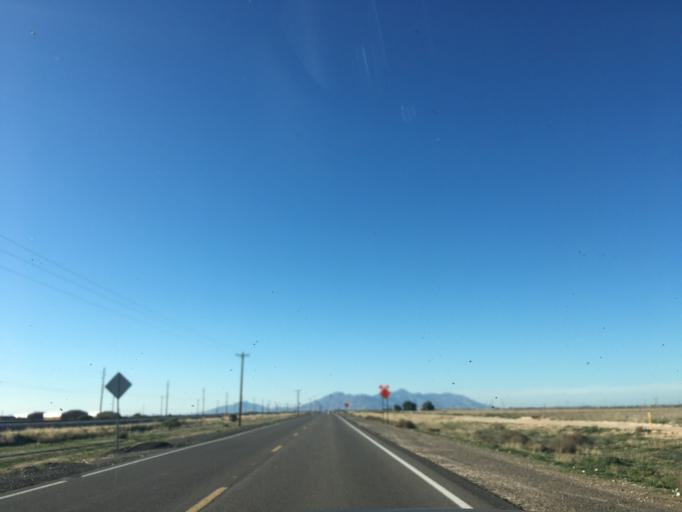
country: US
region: Arizona
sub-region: Pinal County
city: Maricopa
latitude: 33.0163
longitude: -111.9823
